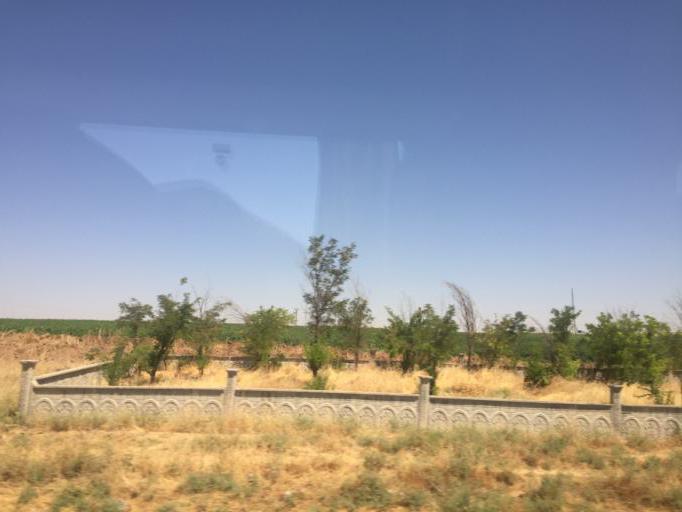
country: TR
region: Diyarbakir
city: Tepe
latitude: 37.8471
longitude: 40.8087
